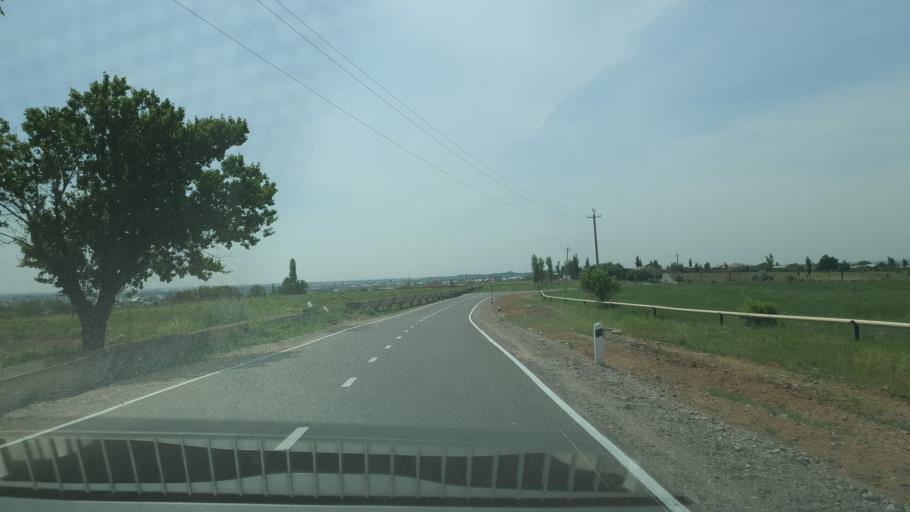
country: UZ
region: Toshkent
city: Salor
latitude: 41.4472
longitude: 69.3750
